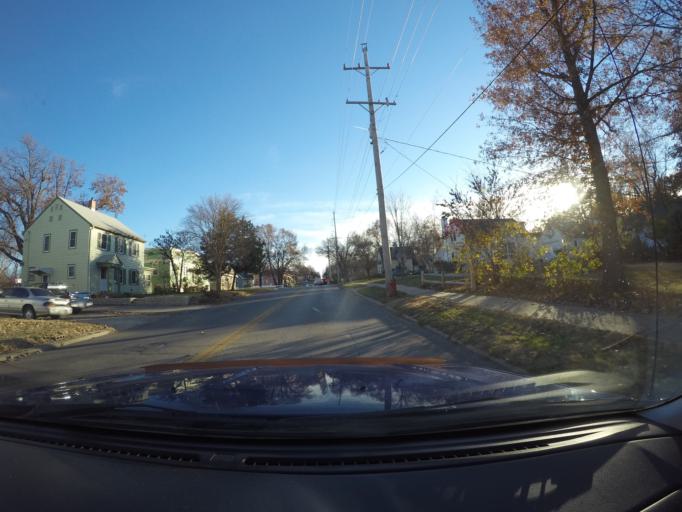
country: US
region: Kansas
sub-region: Riley County
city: Manhattan
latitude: 39.1876
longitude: -96.5888
